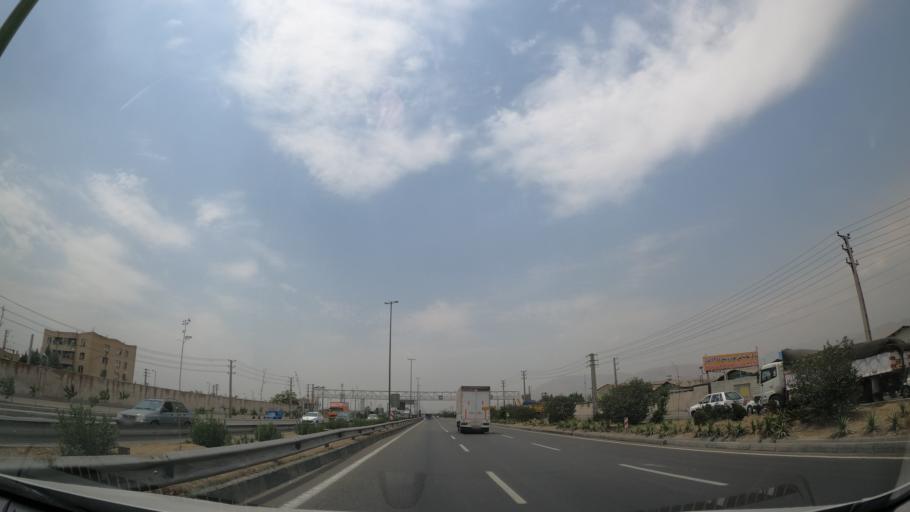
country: IR
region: Tehran
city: Shahr-e Qods
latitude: 35.6966
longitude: 51.2007
